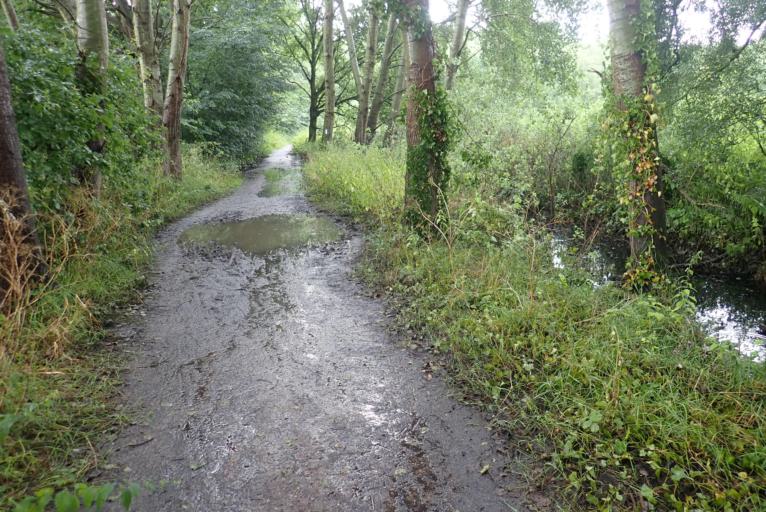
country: BE
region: Flanders
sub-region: Provincie Vlaams-Brabant
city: Tremelo
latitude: 50.9797
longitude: 4.6947
